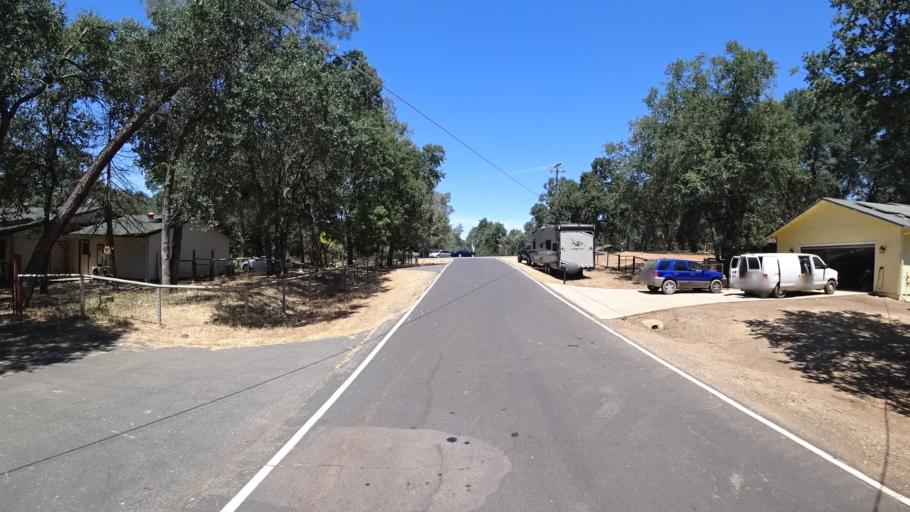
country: US
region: California
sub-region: Calaveras County
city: Rancho Calaveras
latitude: 38.1177
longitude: -120.8605
